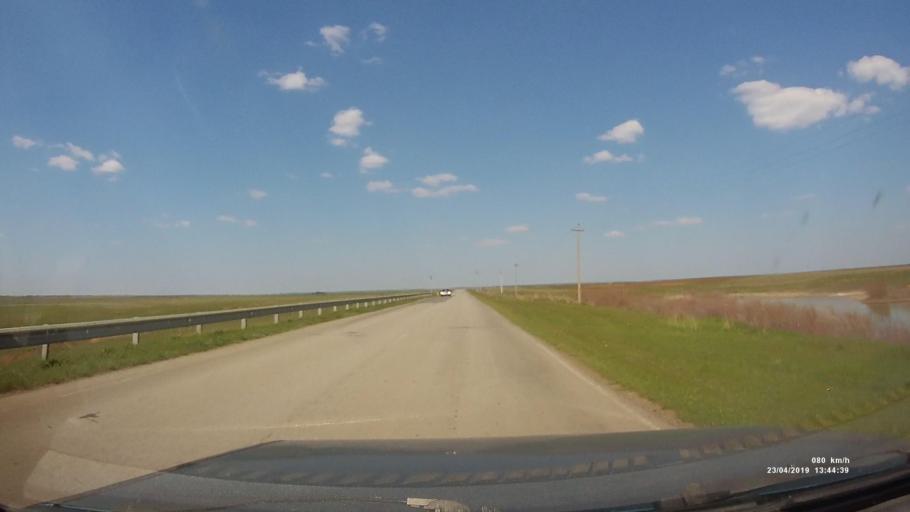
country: RU
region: Kalmykiya
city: Yashalta
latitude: 46.5835
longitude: 42.8174
